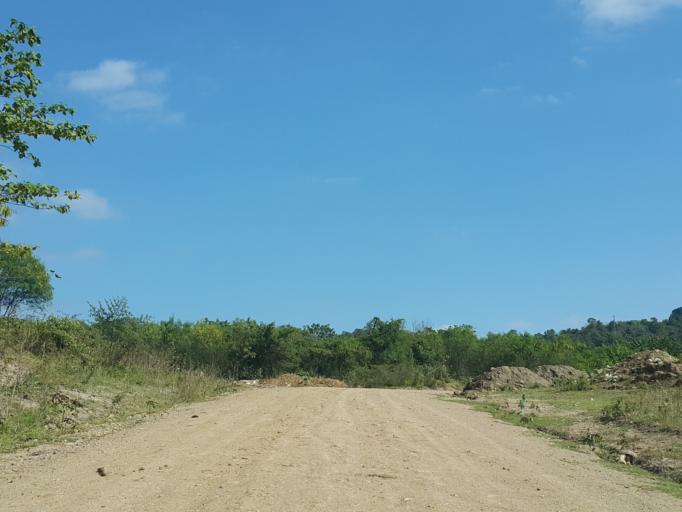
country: TH
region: Lampang
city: Mae Mo
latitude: 18.3304
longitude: 99.7577
